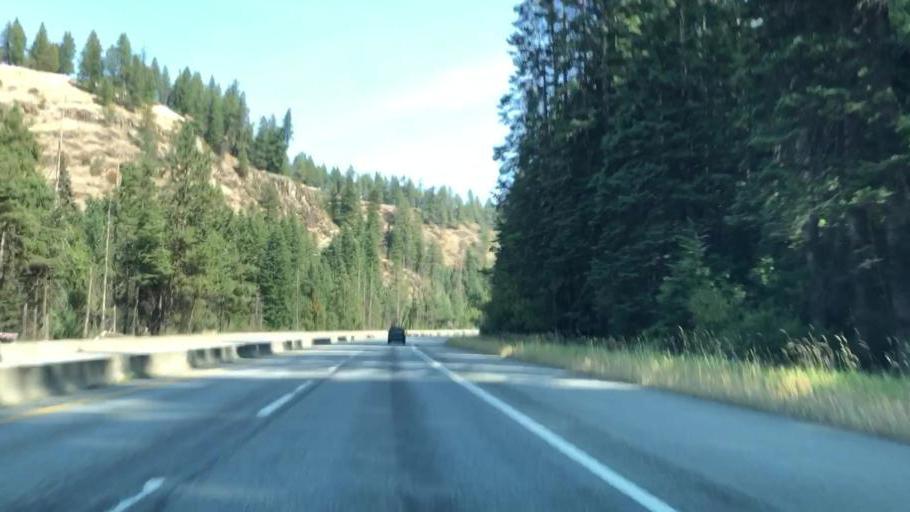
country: US
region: Idaho
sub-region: Kootenai County
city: Coeur d'Alene
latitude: 47.6304
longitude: -116.6046
